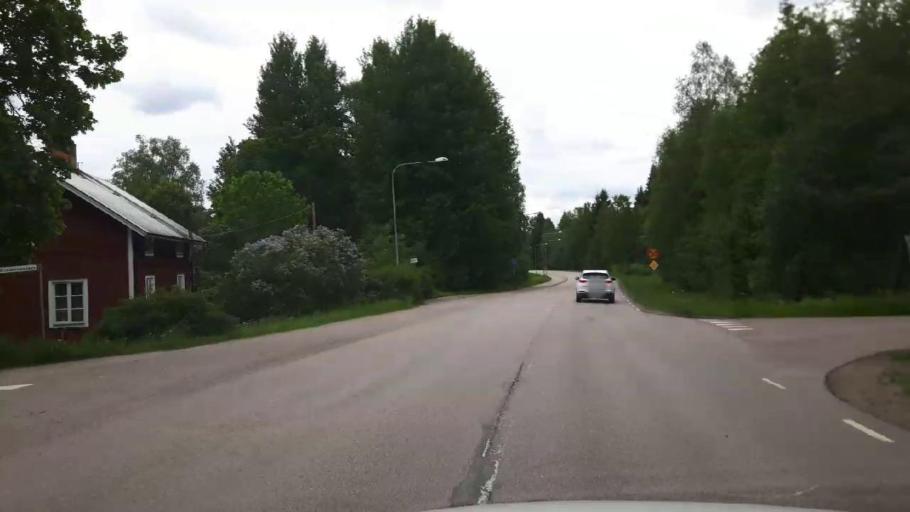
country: SE
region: Vaestmanland
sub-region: Norbergs Kommun
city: Norberg
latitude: 60.0886
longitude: 15.9364
